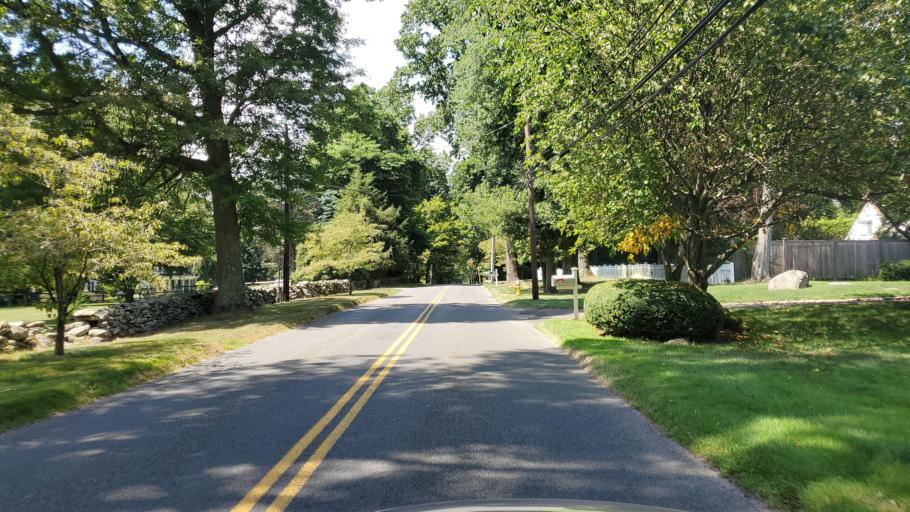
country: US
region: Connecticut
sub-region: Fairfield County
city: Southport
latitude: 41.1679
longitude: -73.2950
